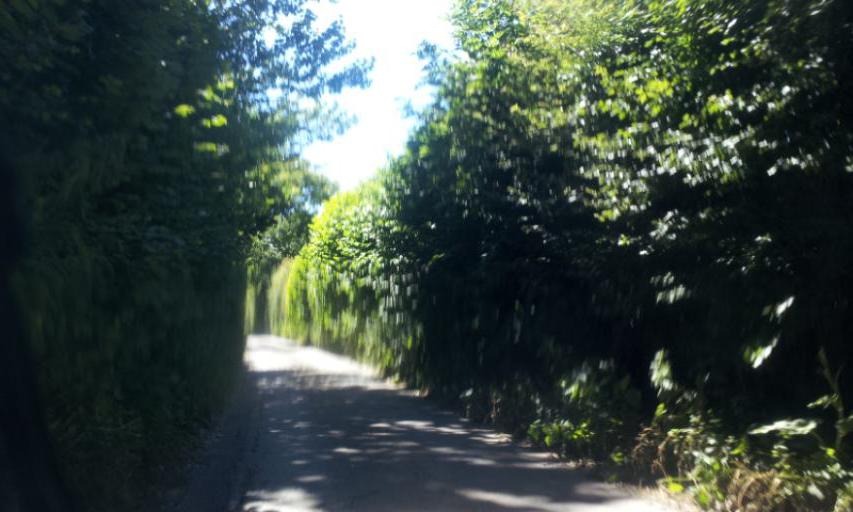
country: GB
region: England
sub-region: Kent
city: Newington
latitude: 51.3305
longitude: 0.6844
